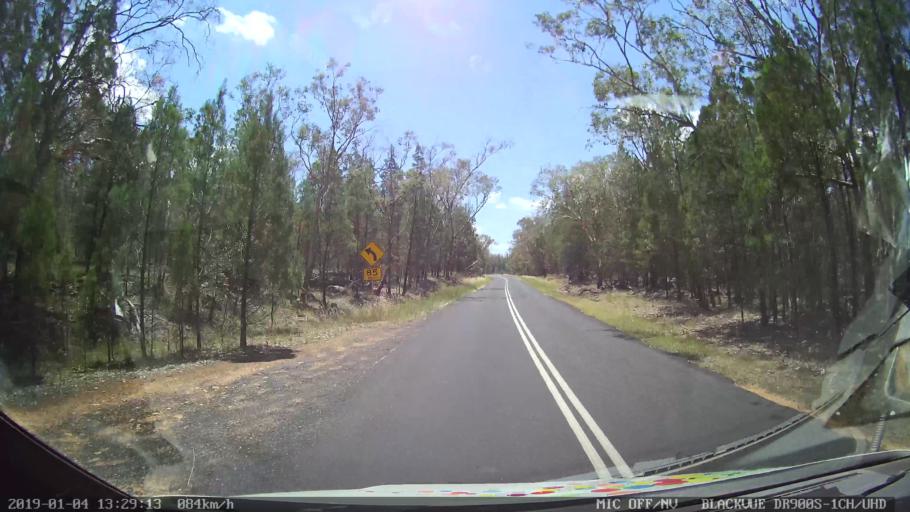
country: AU
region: New South Wales
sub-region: Parkes
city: Peak Hill
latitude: -32.6493
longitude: 148.5508
